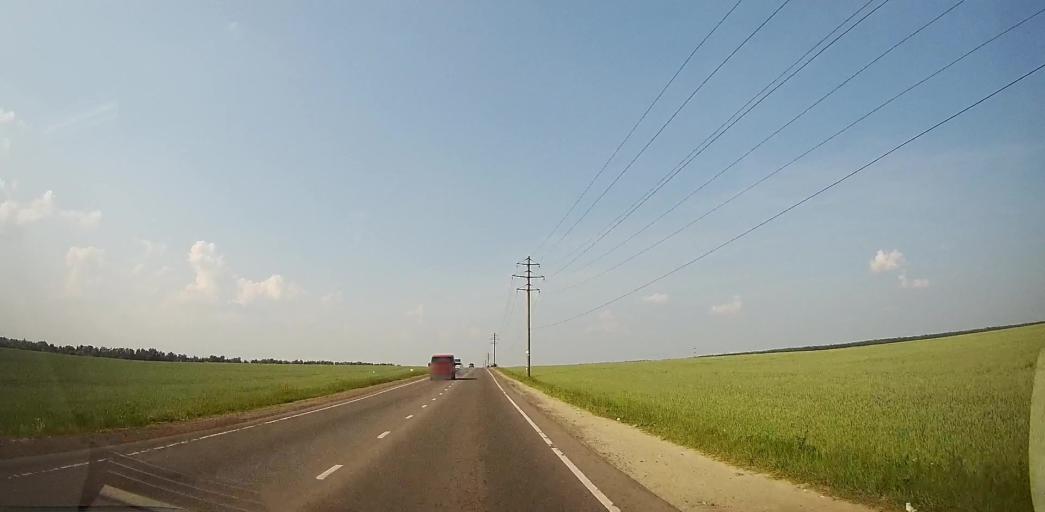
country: RU
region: Moskovskaya
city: Barybino
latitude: 55.2527
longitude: 37.9185
